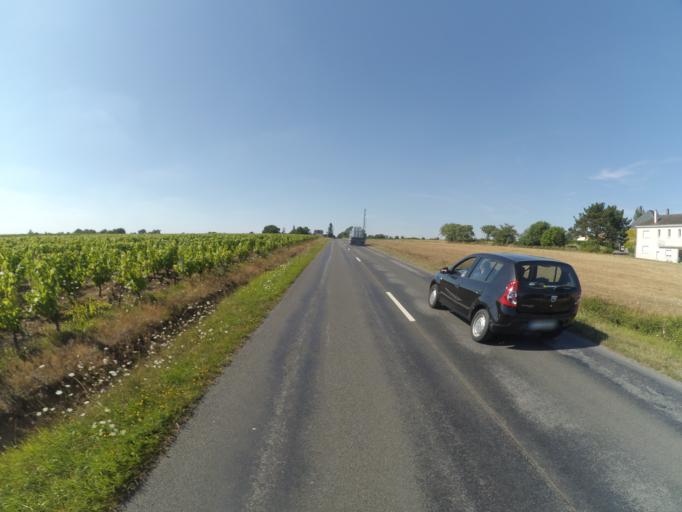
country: FR
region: Pays de la Loire
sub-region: Departement de la Loire-Atlantique
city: Vallet
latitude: 47.1691
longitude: -1.2742
